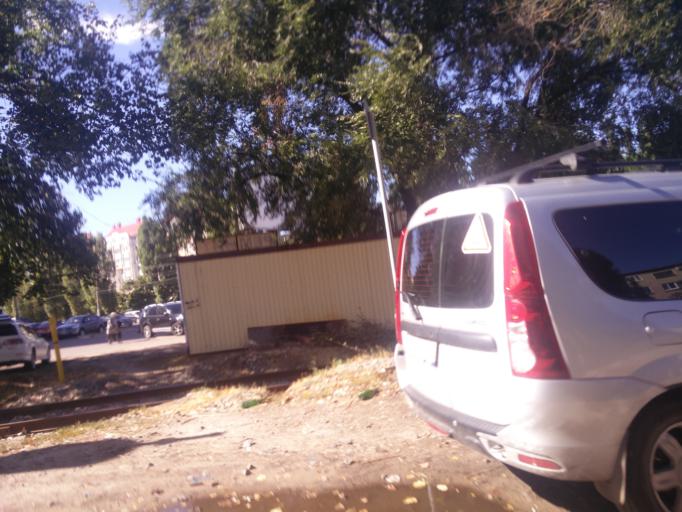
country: RU
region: Voronezj
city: Voronezh
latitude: 51.6487
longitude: 39.1603
